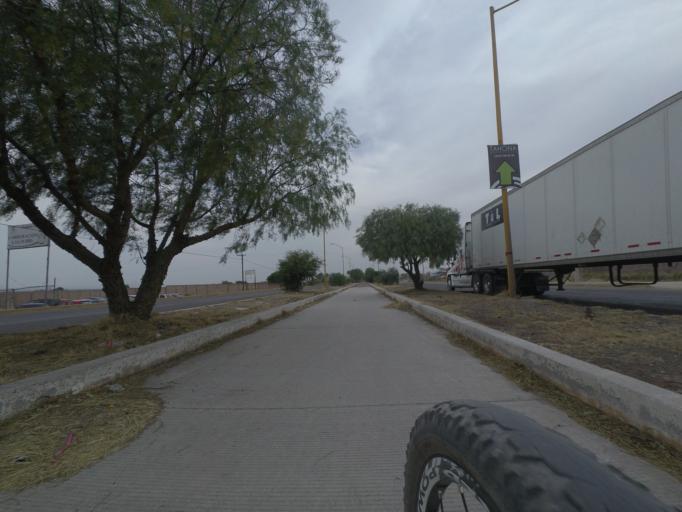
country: MX
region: Aguascalientes
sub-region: Aguascalientes
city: La Loma de los Negritos
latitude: 21.8754
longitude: -102.3699
